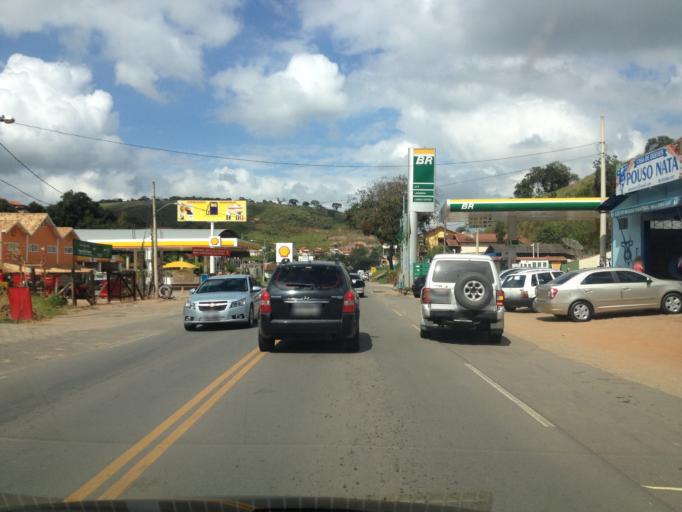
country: BR
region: Minas Gerais
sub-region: Sao Lourenco
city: Sao Lourenco
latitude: -22.1923
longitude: -44.9757
